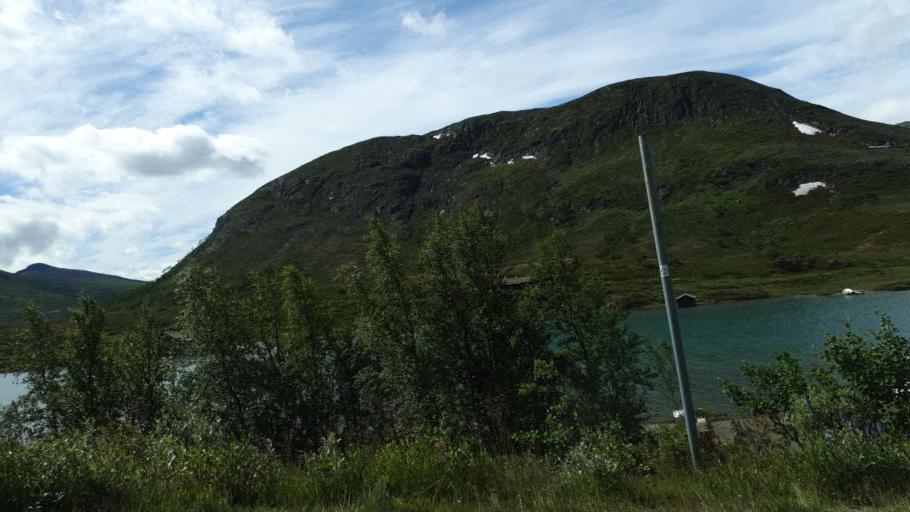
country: NO
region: Oppland
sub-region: Lom
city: Fossbergom
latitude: 61.4949
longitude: 8.8113
